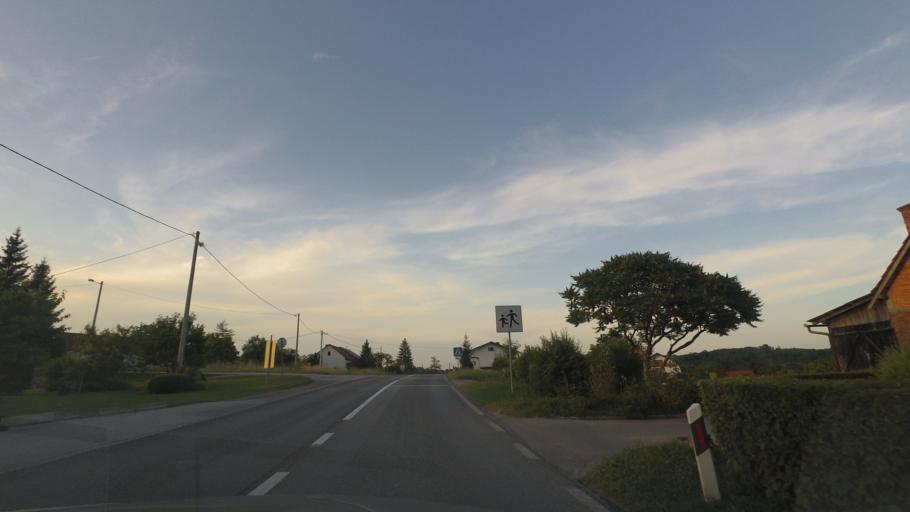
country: HR
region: Karlovacka
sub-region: Grad Karlovac
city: Karlovac
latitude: 45.4070
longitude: 15.4482
